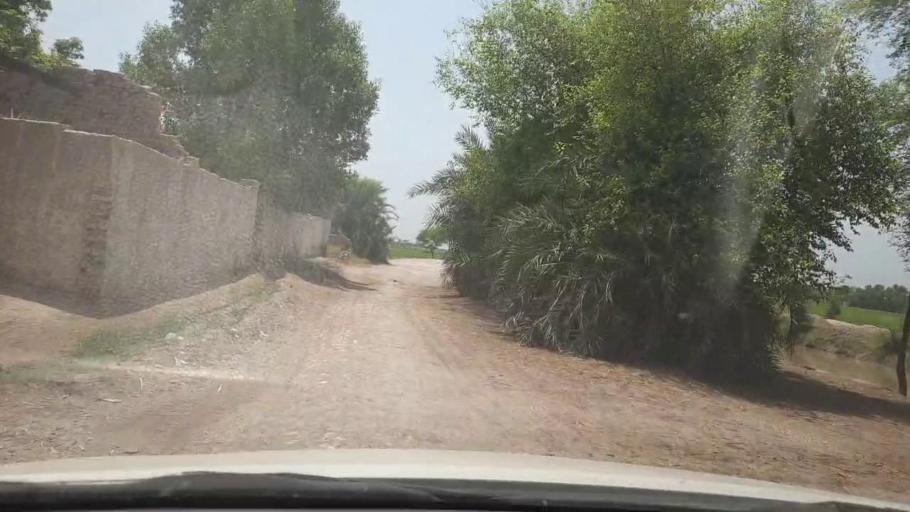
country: PK
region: Sindh
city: Shikarpur
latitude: 28.0934
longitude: 68.5765
